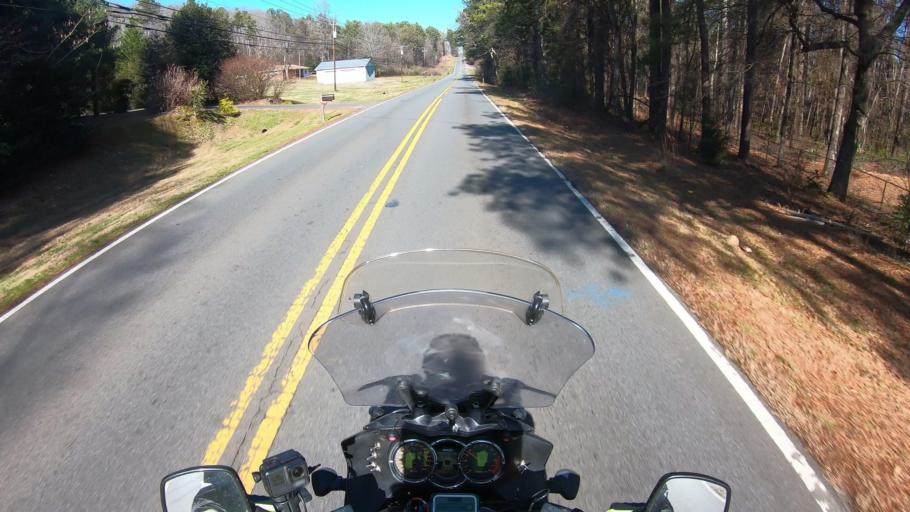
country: US
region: Georgia
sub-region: Bartow County
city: Cartersville
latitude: 34.2494
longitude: -84.8083
